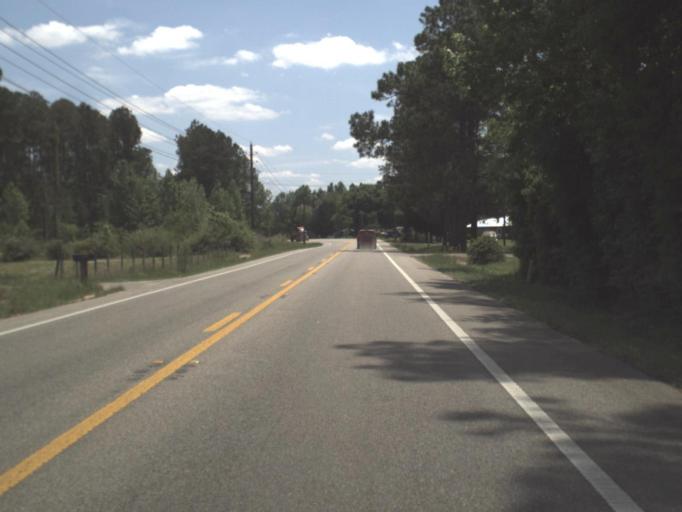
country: US
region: Florida
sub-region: Calhoun County
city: Blountstown
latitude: 30.4730
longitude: -85.0926
